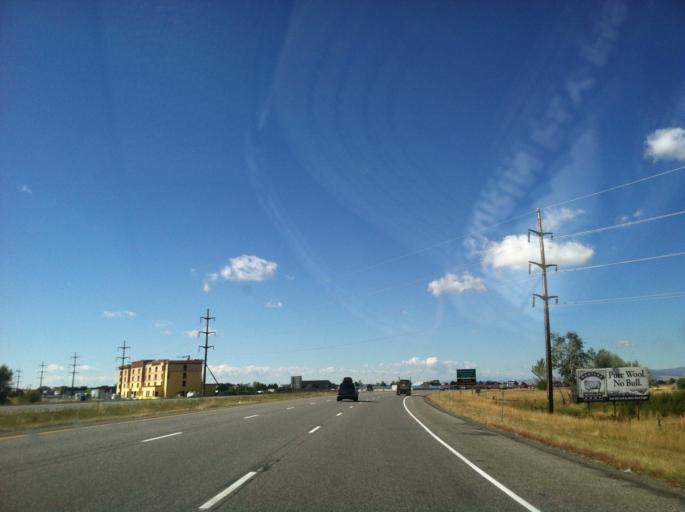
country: US
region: Montana
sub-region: Gallatin County
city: Bozeman
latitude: 45.7001
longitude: -111.0553
